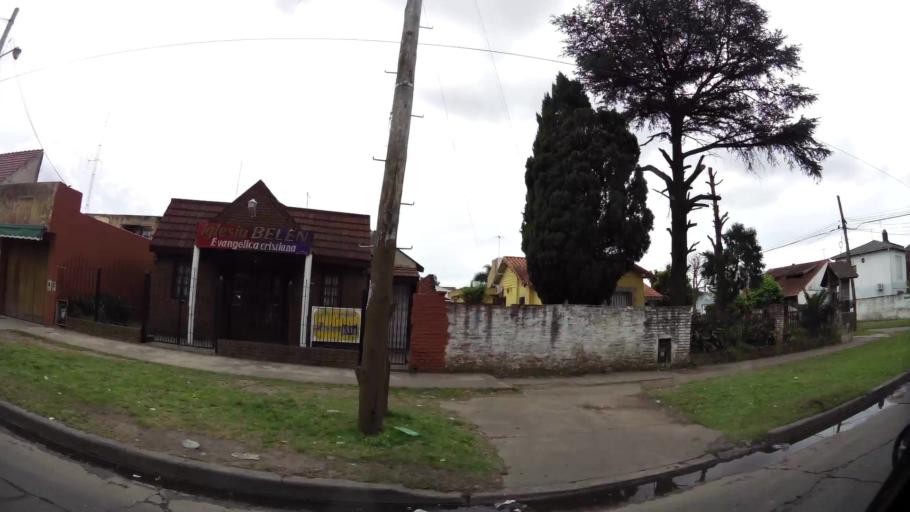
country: AR
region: Buenos Aires
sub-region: Partido de Quilmes
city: Quilmes
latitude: -34.7677
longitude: -58.2799
